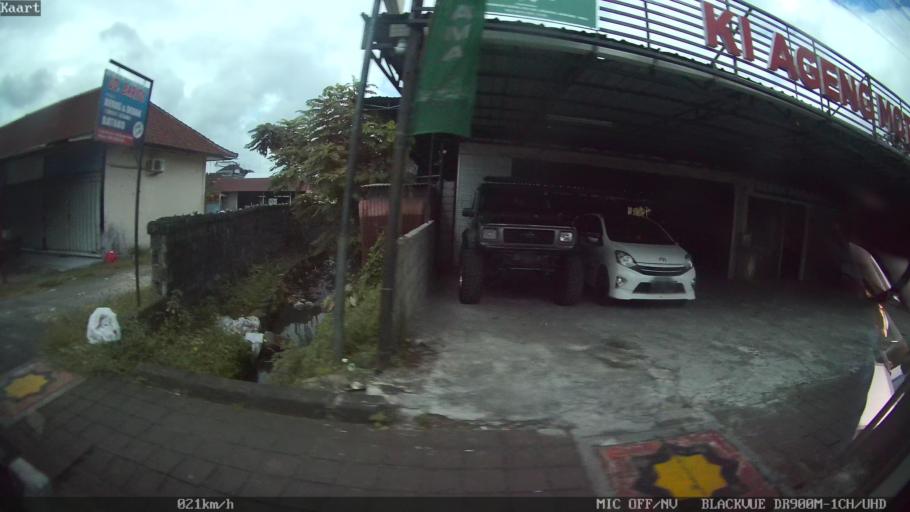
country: ID
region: Bali
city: Banjar Karangsuling
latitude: -8.5971
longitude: 115.1737
